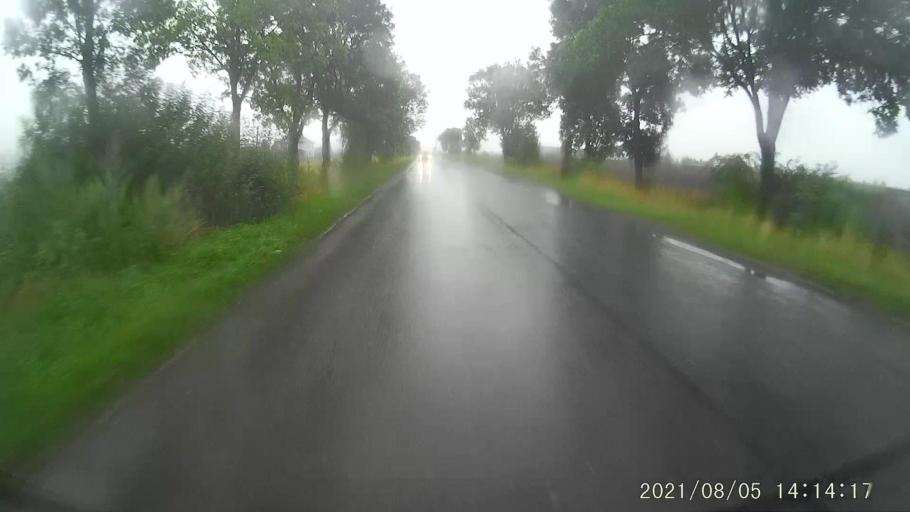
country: PL
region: Opole Voivodeship
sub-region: Powiat krapkowicki
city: Strzeleczki
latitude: 50.4692
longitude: 17.7417
